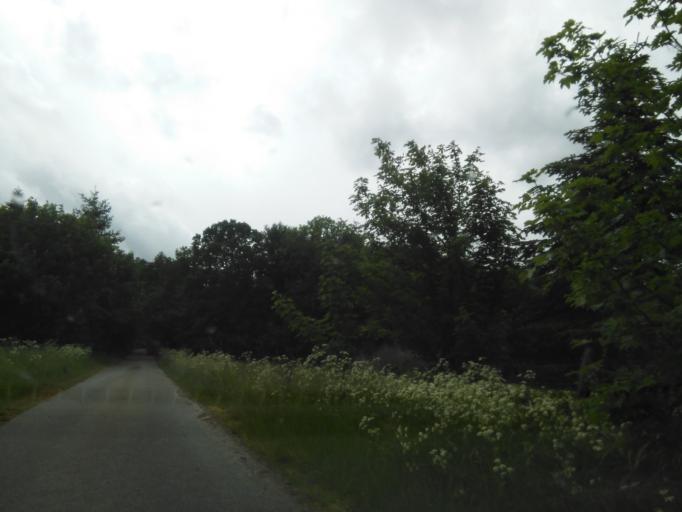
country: DK
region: Capital Region
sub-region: Bornholm Kommune
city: Nexo
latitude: 55.0953
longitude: 15.1134
